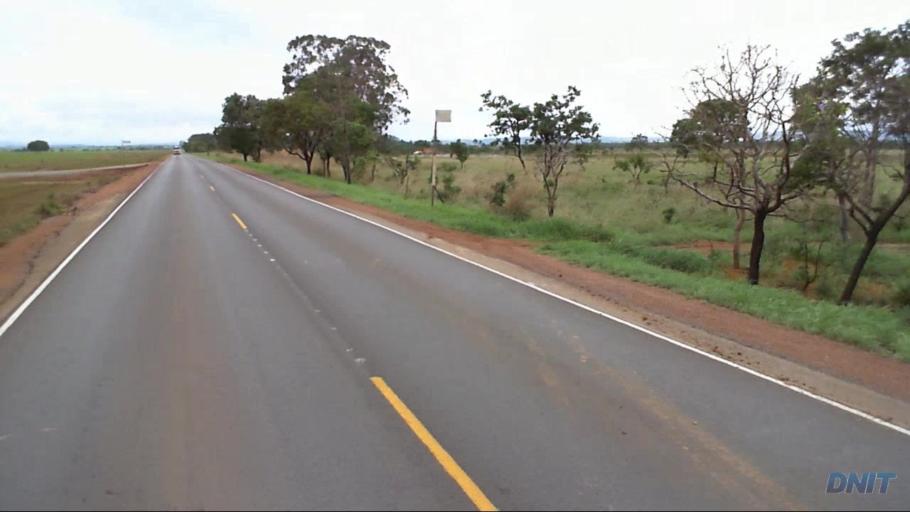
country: BR
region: Goias
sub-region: Padre Bernardo
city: Padre Bernardo
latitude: -15.3340
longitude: -48.2329
